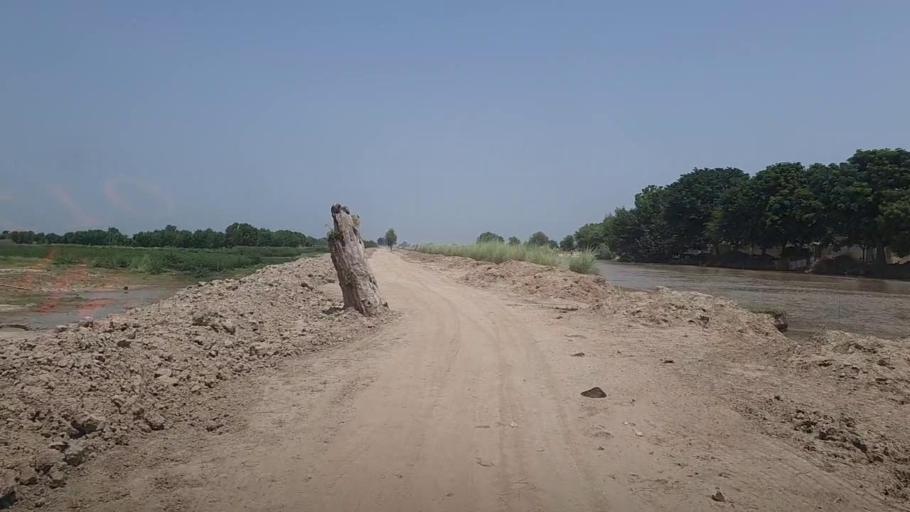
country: PK
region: Sindh
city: Pad Idan
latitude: 26.7849
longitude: 68.2777
